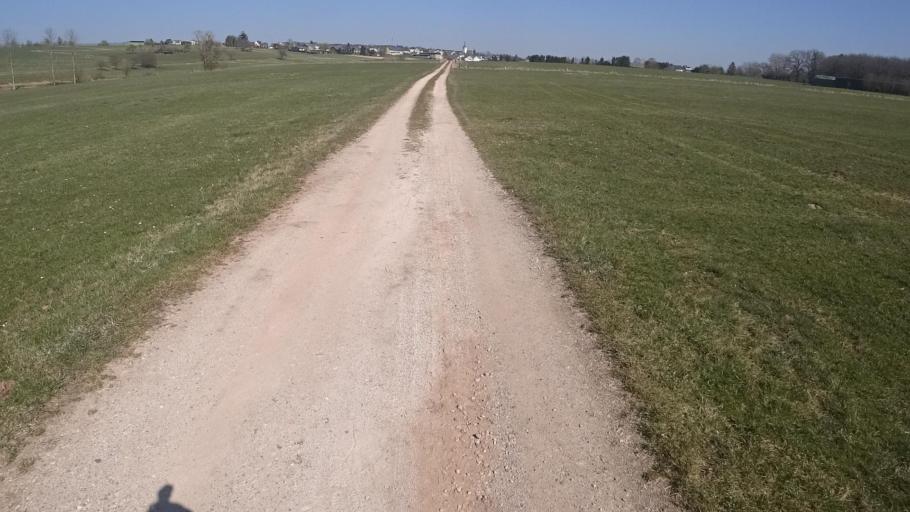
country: DE
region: Rheinland-Pfalz
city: Argenthal
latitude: 49.9679
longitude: 7.5850
